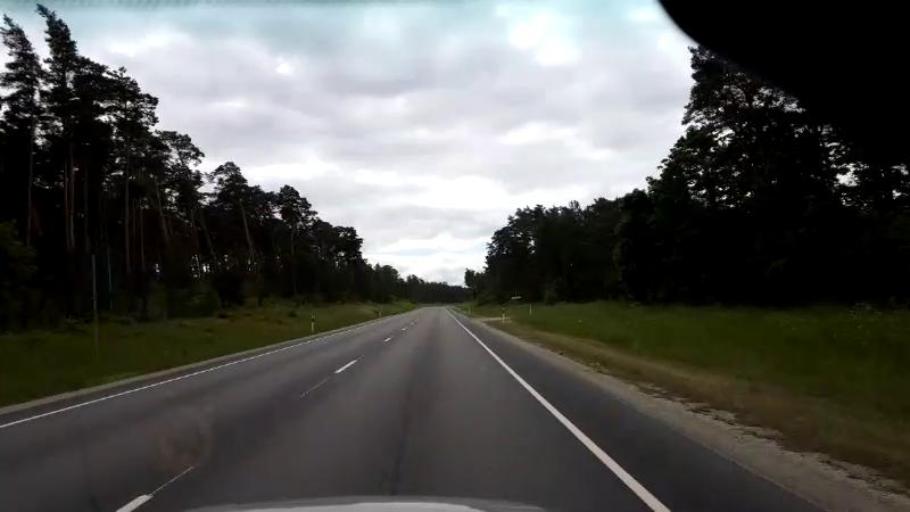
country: EE
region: Paernumaa
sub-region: Paernu linn
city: Parnu
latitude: 58.1913
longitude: 24.4904
